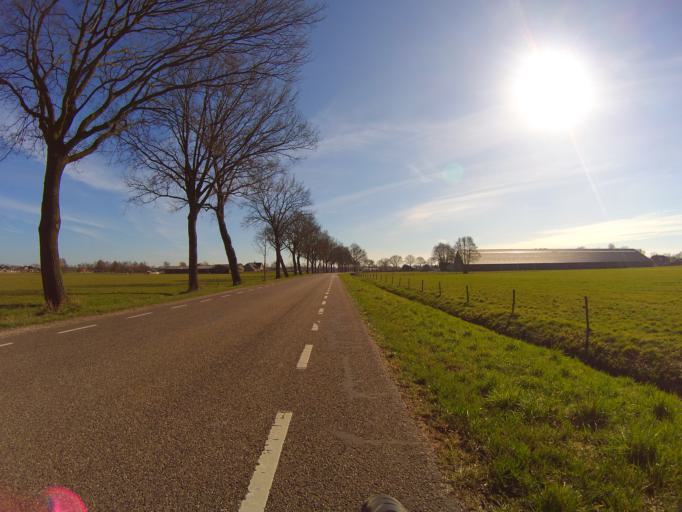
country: NL
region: Utrecht
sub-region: Gemeente Utrechtse Heuvelrug
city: Overberg
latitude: 52.0601
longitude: 5.5002
